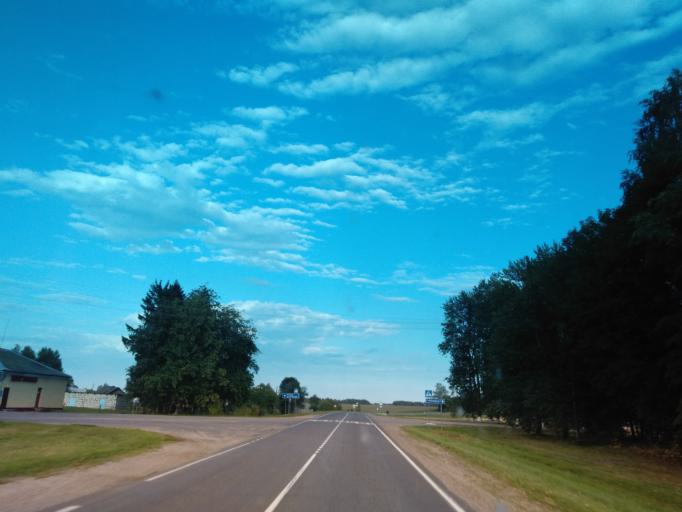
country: BY
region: Minsk
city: Uzda
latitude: 53.4376
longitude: 27.3271
